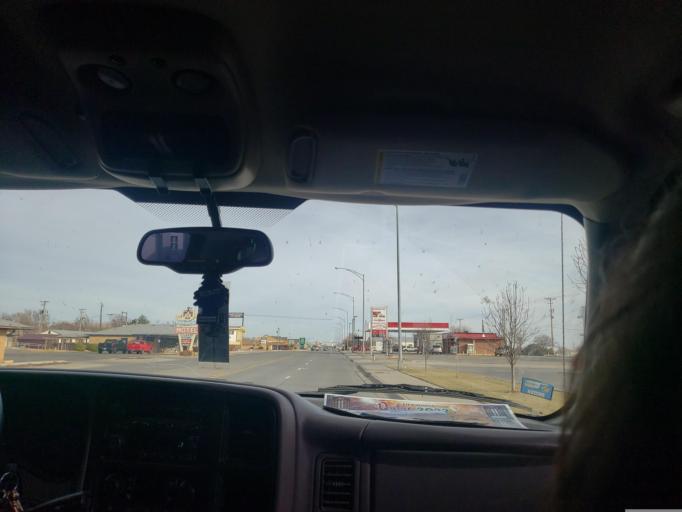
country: US
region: Kansas
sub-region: Ford County
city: Dodge City
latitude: 37.7543
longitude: -100.0457
